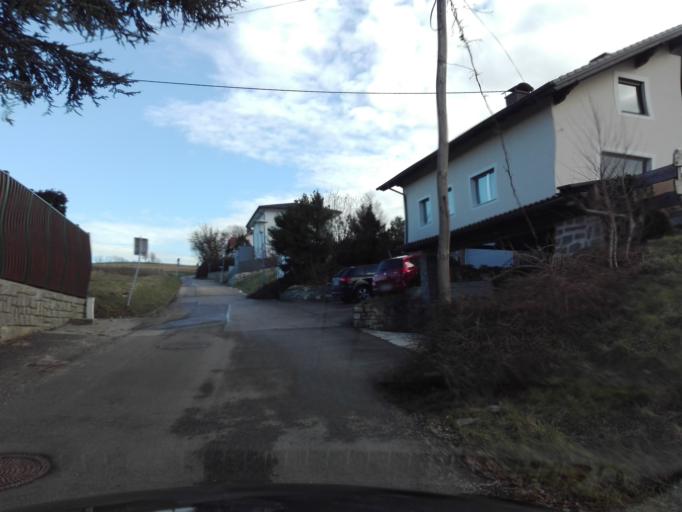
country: AT
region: Upper Austria
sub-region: Politischer Bezirk Perg
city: Perg
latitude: 48.2714
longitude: 14.5870
